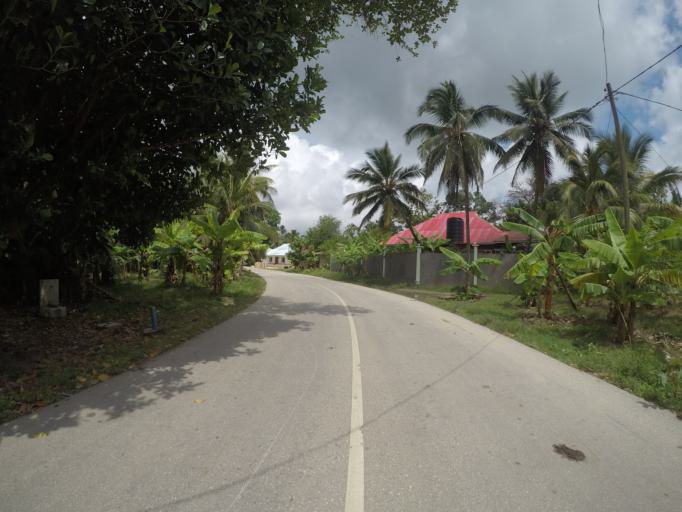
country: TZ
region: Pemba South
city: Mtambile
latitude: -5.3872
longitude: 39.7464
